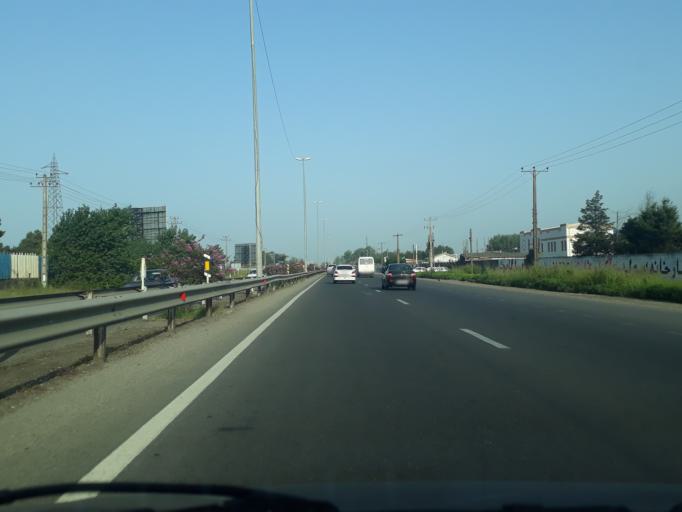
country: IR
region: Gilan
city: Bandar-e Anzali
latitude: 37.4591
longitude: 49.5973
